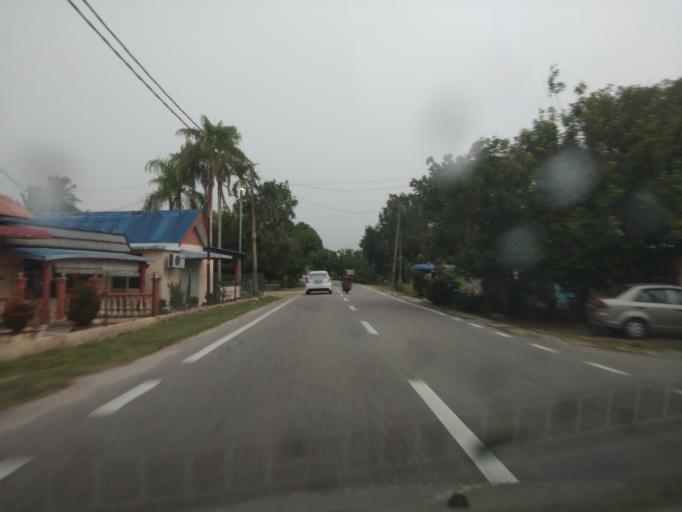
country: MY
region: Penang
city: Permatang Kuching
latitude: 5.4846
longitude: 100.4008
